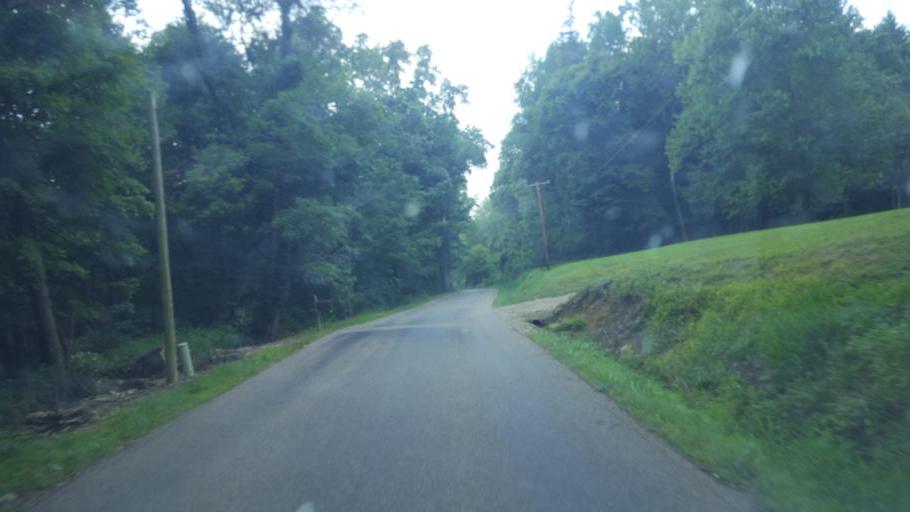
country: US
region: Ohio
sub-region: Knox County
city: Mount Vernon
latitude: 40.3699
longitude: -82.4537
